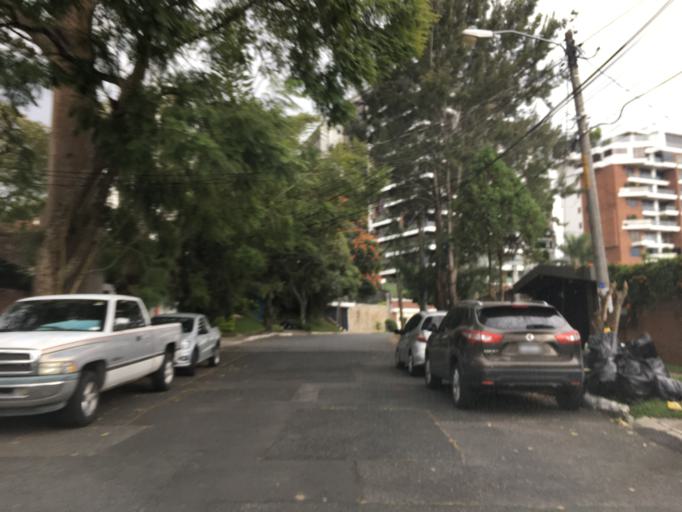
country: GT
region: Guatemala
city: Santa Catarina Pinula
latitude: 14.5859
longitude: -90.4896
